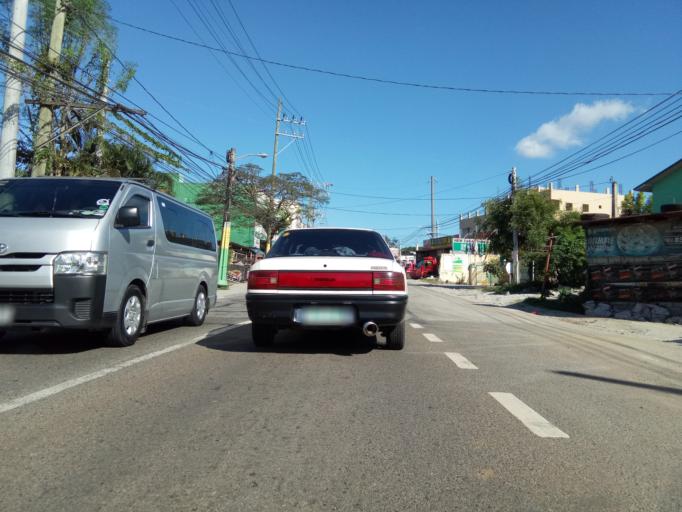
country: PH
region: Calabarzon
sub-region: Province of Cavite
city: Dasmarinas
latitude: 14.3522
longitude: 120.9464
